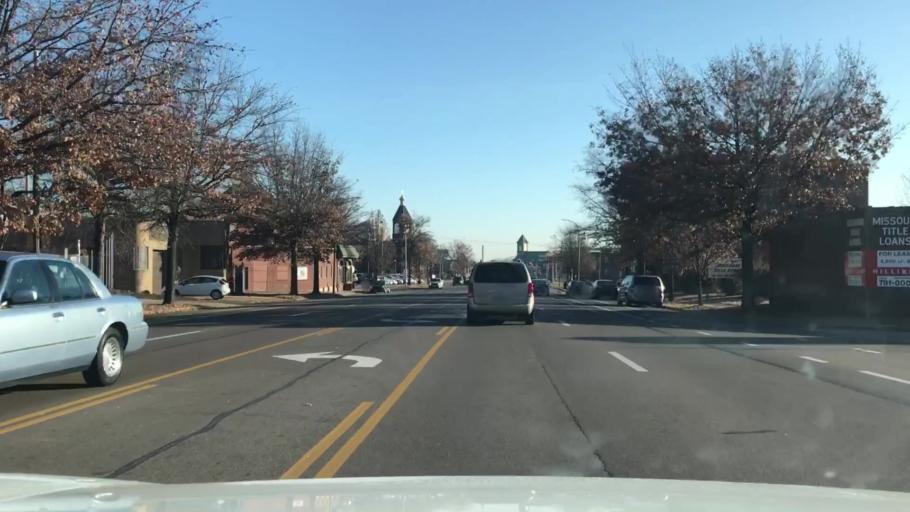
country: US
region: Missouri
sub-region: City of Saint Louis
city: St. Louis
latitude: 38.6072
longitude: -90.2165
